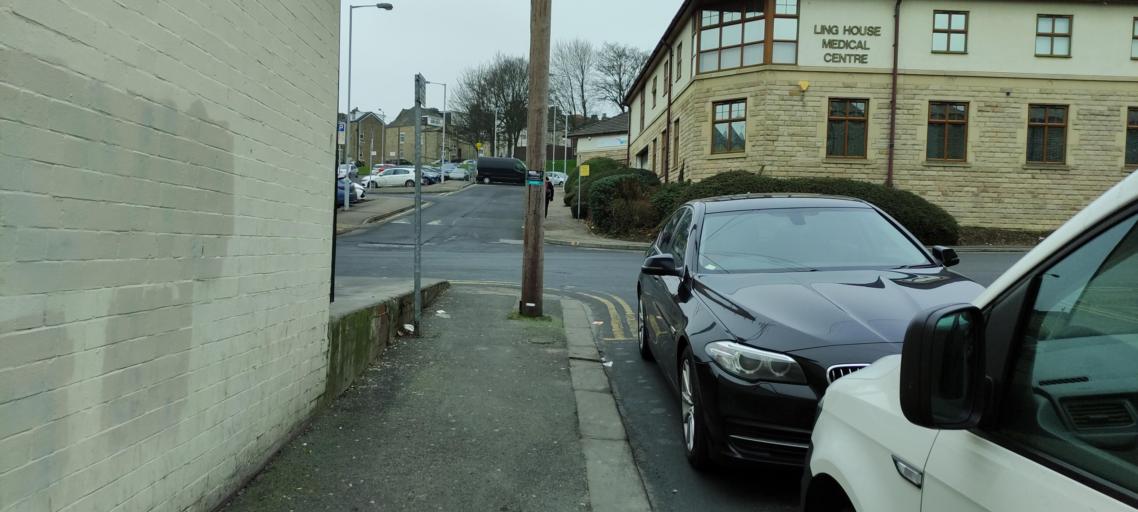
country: GB
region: England
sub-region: Bradford
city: Keighley
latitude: 53.8694
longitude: -1.9101
